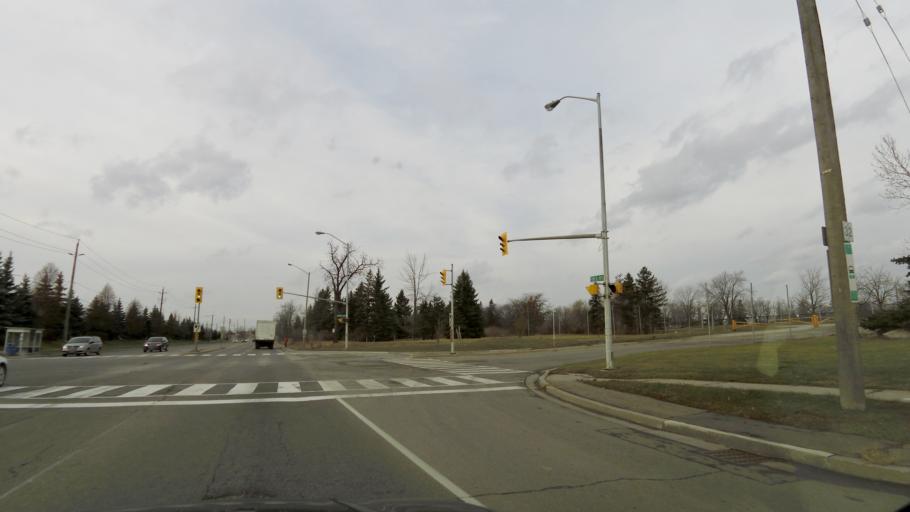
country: CA
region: Ontario
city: Etobicoke
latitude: 43.7398
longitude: -79.6432
